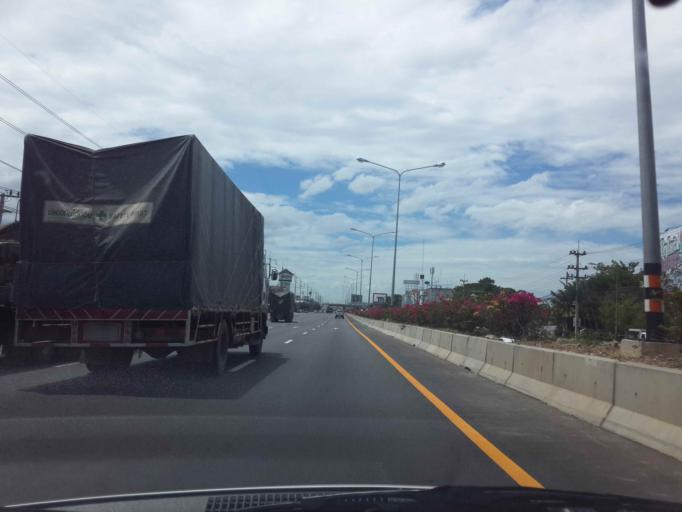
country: TH
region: Phetchaburi
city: Phetchaburi
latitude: 13.1049
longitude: 99.9347
